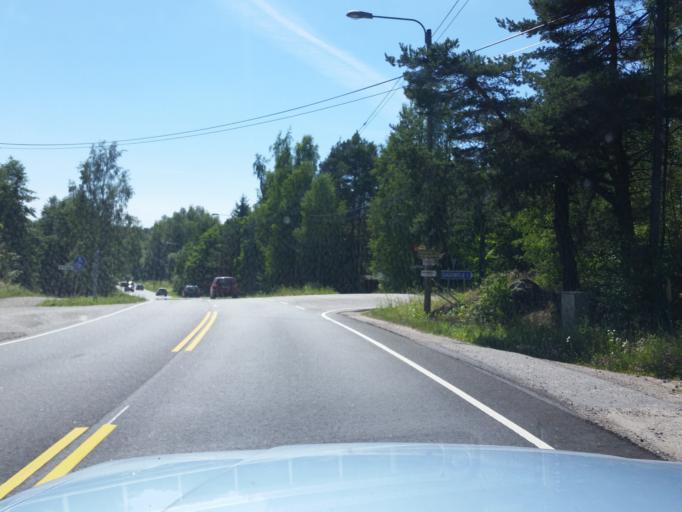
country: FI
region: Varsinais-Suomi
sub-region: Aboland-Turunmaa
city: Laensi-Turunmaa
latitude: 60.2829
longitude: 22.2470
